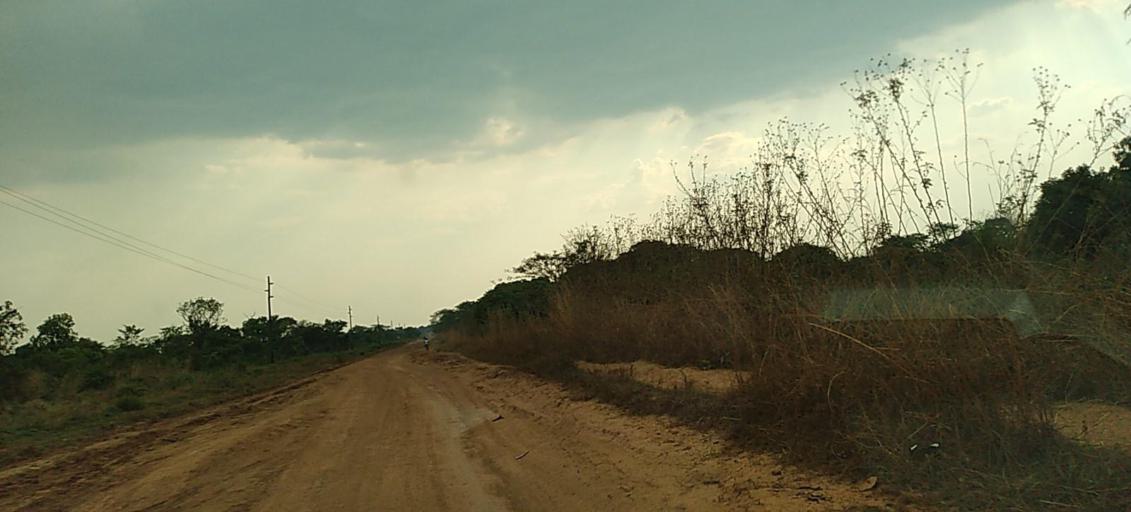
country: ZM
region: Copperbelt
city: Kalulushi
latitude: -12.9485
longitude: 27.9129
